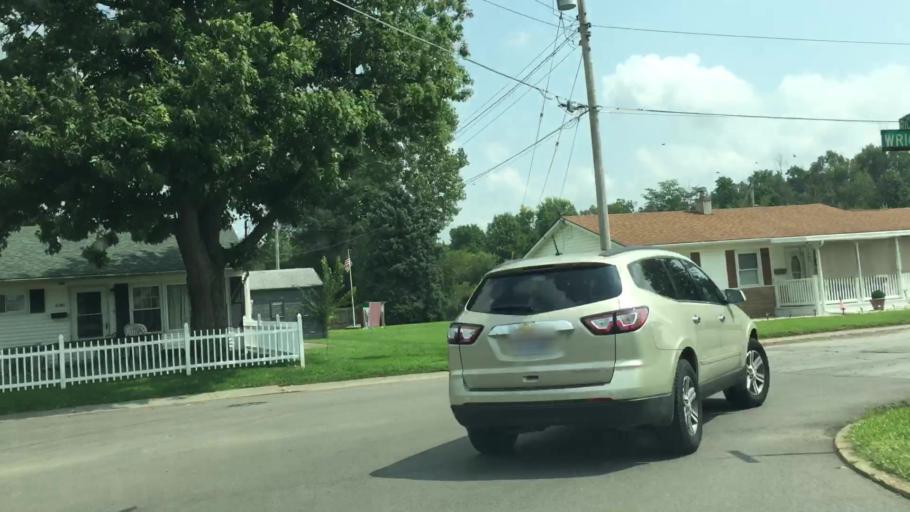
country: US
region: Ohio
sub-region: Logan County
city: Bellefontaine
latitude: 40.3417
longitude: -83.7596
